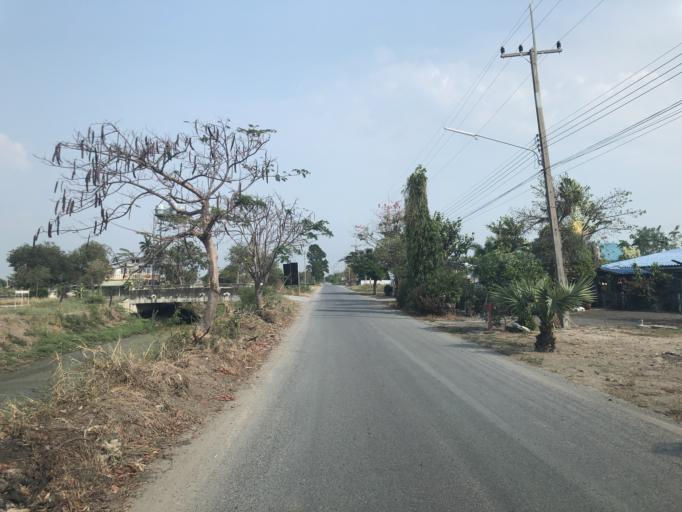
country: TH
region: Chachoengsao
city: Bang Pakong
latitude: 13.5106
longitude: 100.9305
